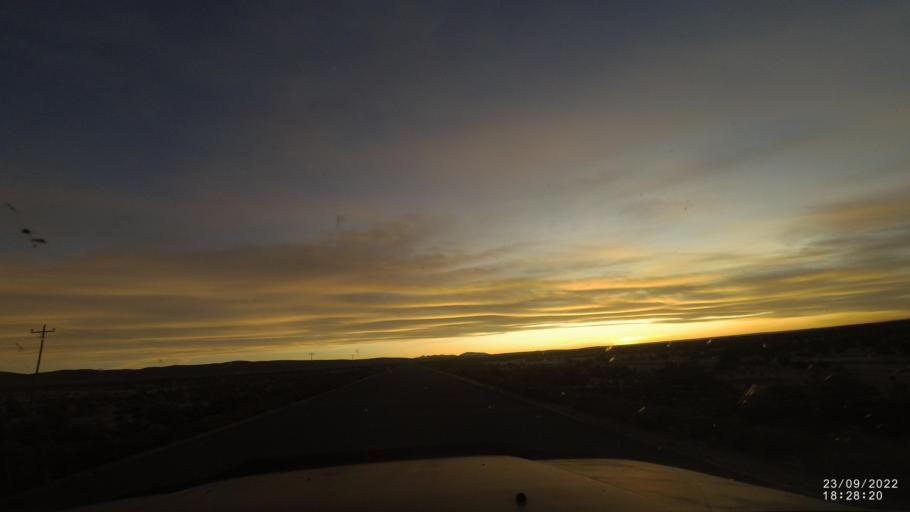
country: BO
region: Oruro
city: Challapata
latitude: -19.3366
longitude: -67.1757
